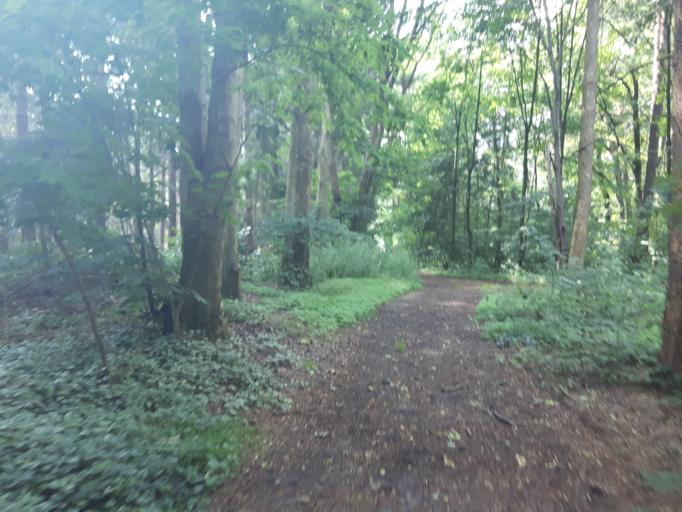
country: NL
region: Overijssel
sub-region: Gemeente Haaksbergen
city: Haaksbergen
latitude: 52.1849
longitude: 6.7632
